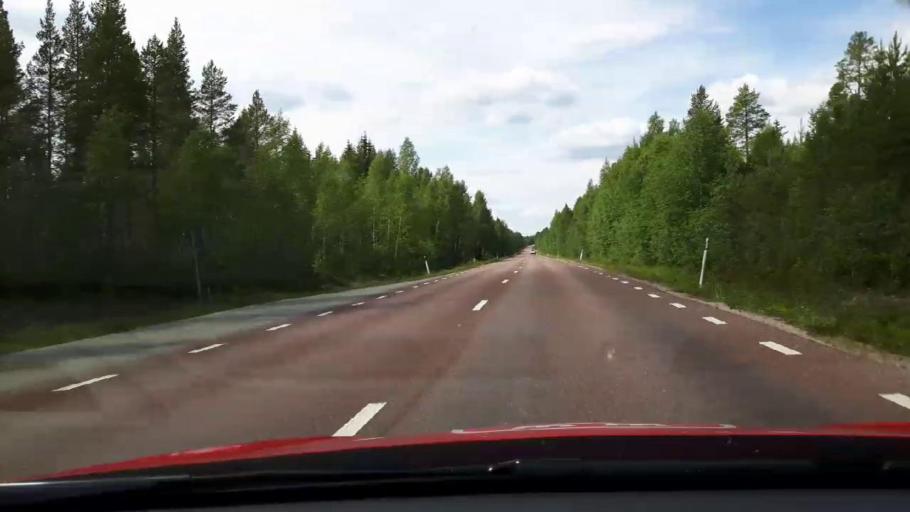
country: SE
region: Jaemtland
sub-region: Harjedalens Kommun
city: Sveg
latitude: 62.0465
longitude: 14.8336
